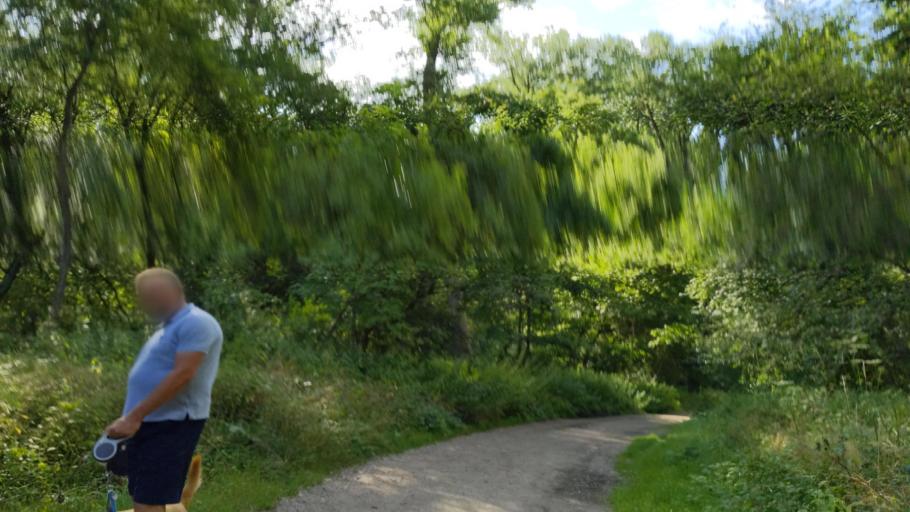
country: DE
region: Schleswig-Holstein
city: Travemuende
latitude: 53.9516
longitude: 10.8764
